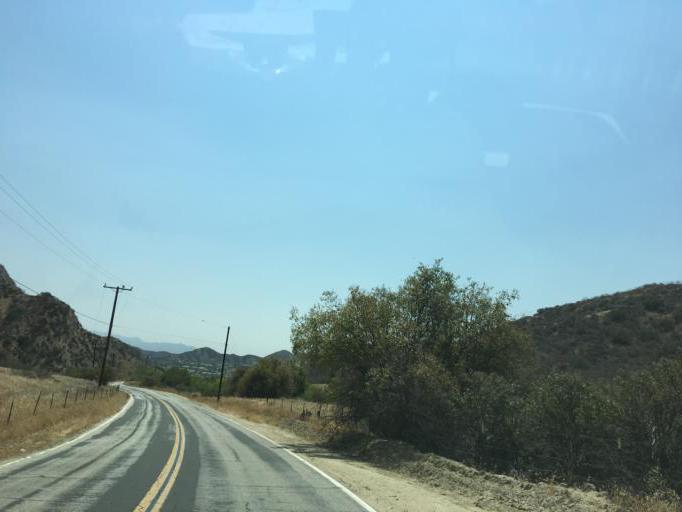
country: US
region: California
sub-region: Los Angeles County
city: Santa Clarita
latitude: 34.3803
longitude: -118.6009
